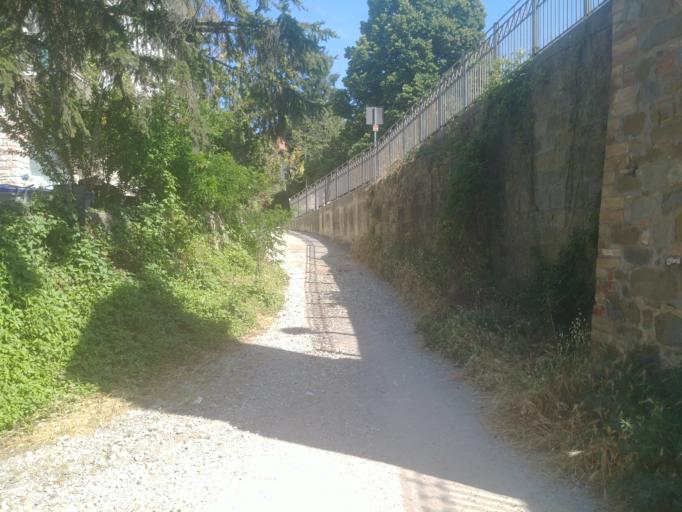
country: IT
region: Umbria
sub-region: Provincia di Perugia
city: Ponte Felcino
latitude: 43.1330
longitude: 12.4429
